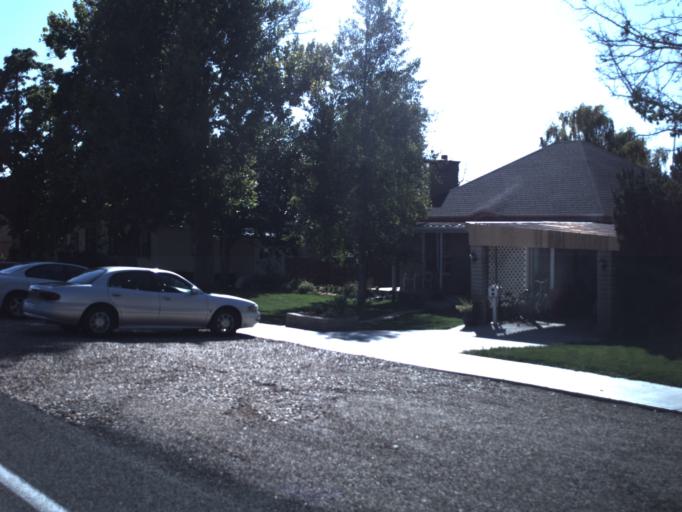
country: US
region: Utah
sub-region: Millard County
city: Fillmore
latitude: 39.1003
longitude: -112.2710
